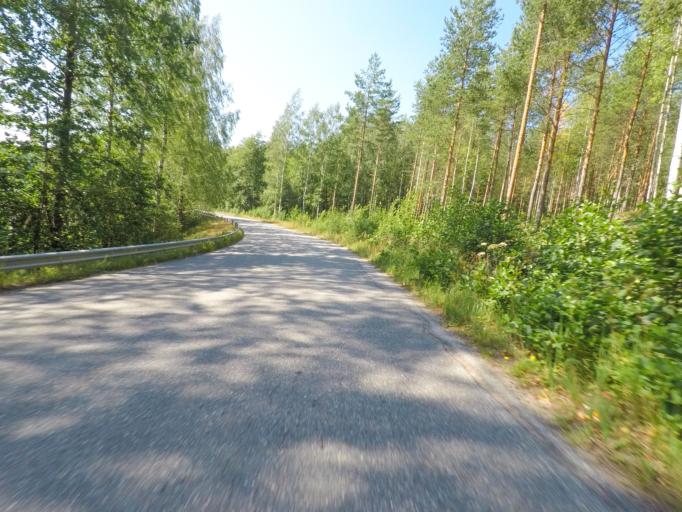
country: FI
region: Southern Savonia
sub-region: Mikkeli
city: Puumala
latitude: 61.4233
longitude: 28.1000
